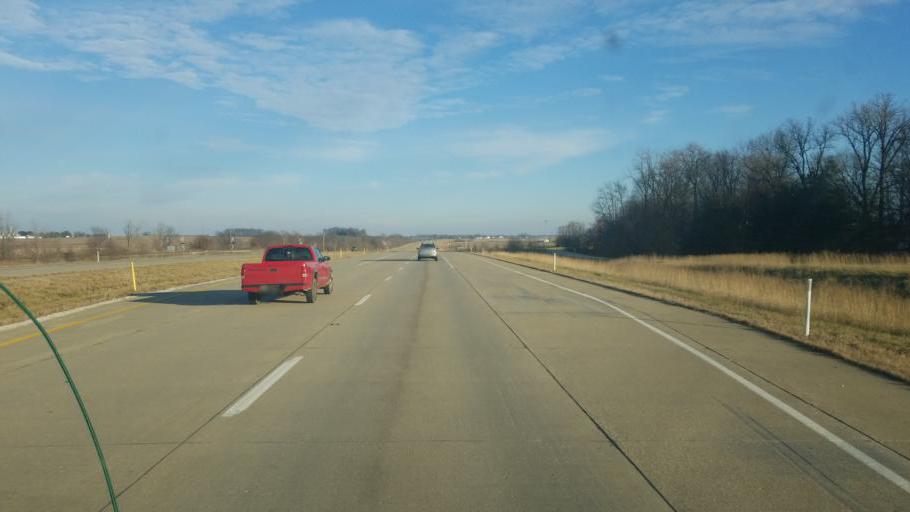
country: US
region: Indiana
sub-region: Knox County
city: Bicknell
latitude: 38.6777
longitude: -87.3910
